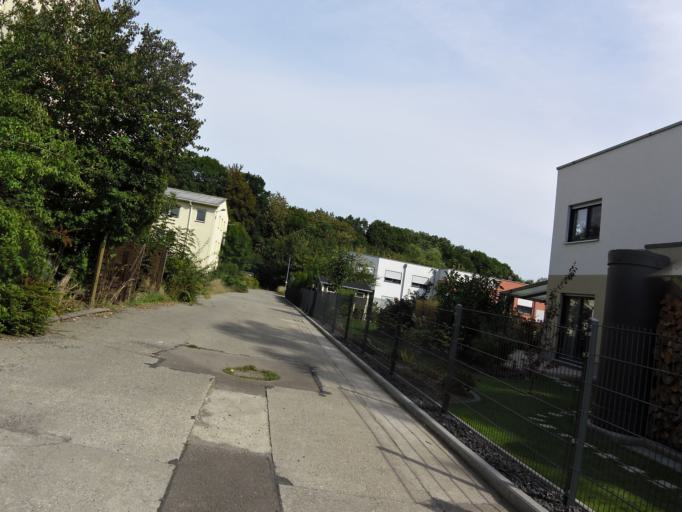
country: DE
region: Saxony
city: Schkeuditz
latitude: 51.3620
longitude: 12.2773
